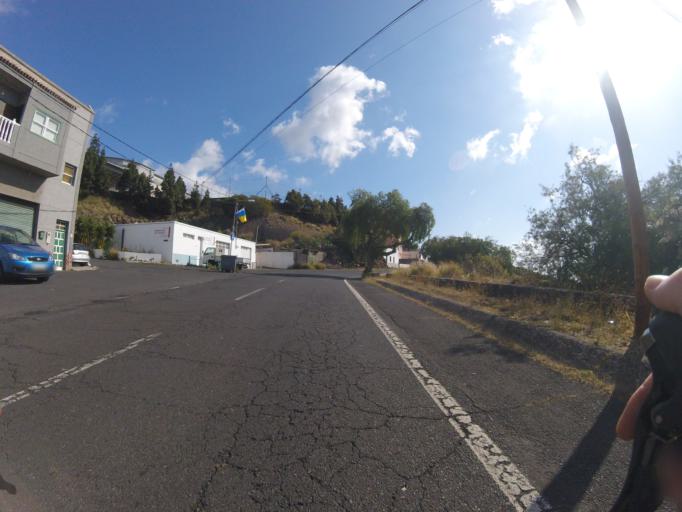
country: ES
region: Canary Islands
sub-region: Provincia de Santa Cruz de Tenerife
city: La Laguna
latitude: 28.4156
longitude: -16.3224
